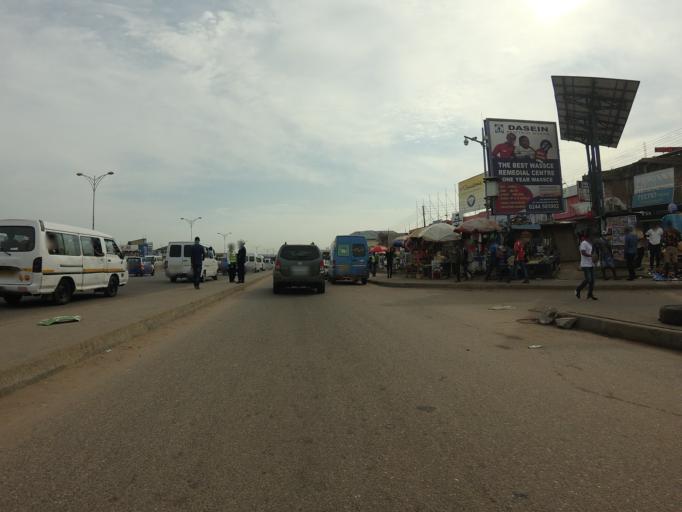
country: GH
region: Greater Accra
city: Dome
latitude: 5.6067
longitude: -0.2486
